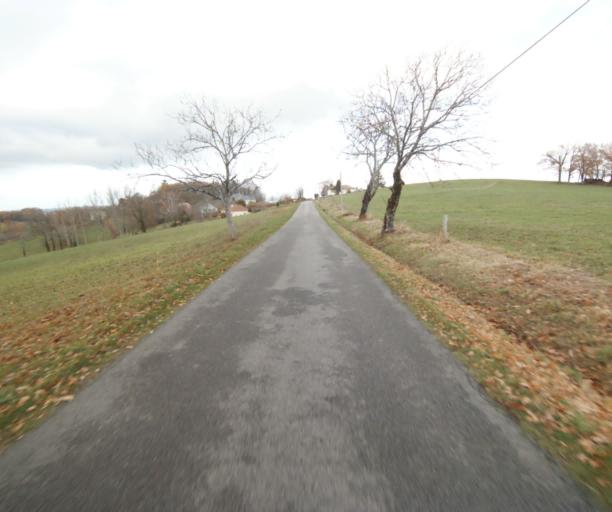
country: FR
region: Limousin
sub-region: Departement de la Correze
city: Sainte-Fortunade
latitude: 45.2132
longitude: 1.7893
